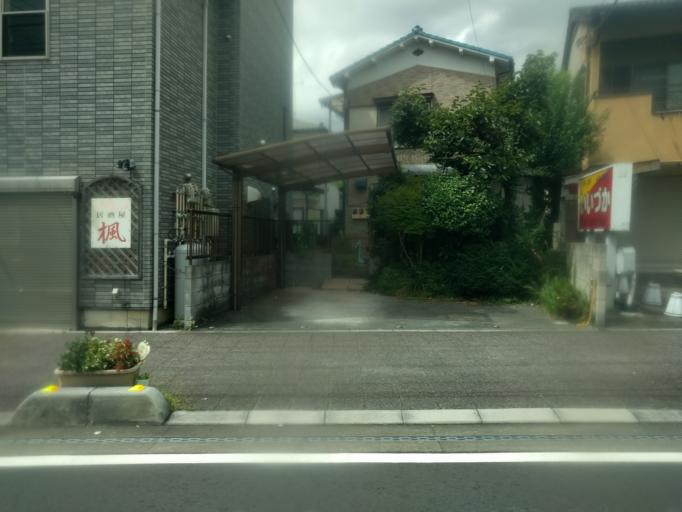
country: JP
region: Saitama
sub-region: Kawaguchi-shi
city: Hatogaya-honcho
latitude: 35.8292
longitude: 139.7393
